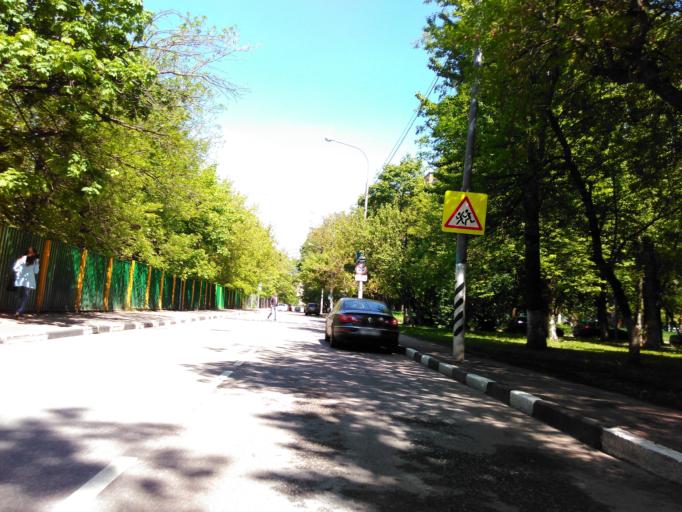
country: RU
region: Moskovskaya
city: Leninskiye Gory
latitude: 55.7005
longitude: 37.5621
